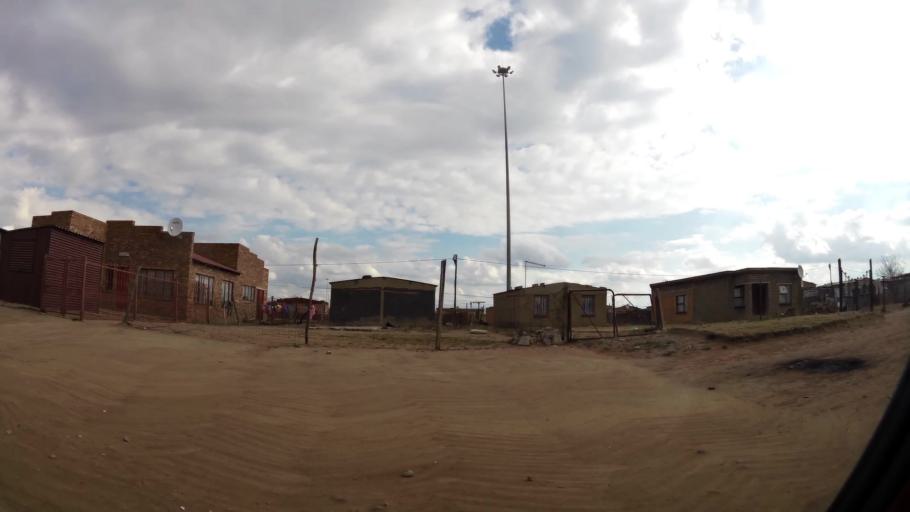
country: ZA
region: Gauteng
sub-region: Sedibeng District Municipality
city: Vanderbijlpark
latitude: -26.6811
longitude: 27.7811
